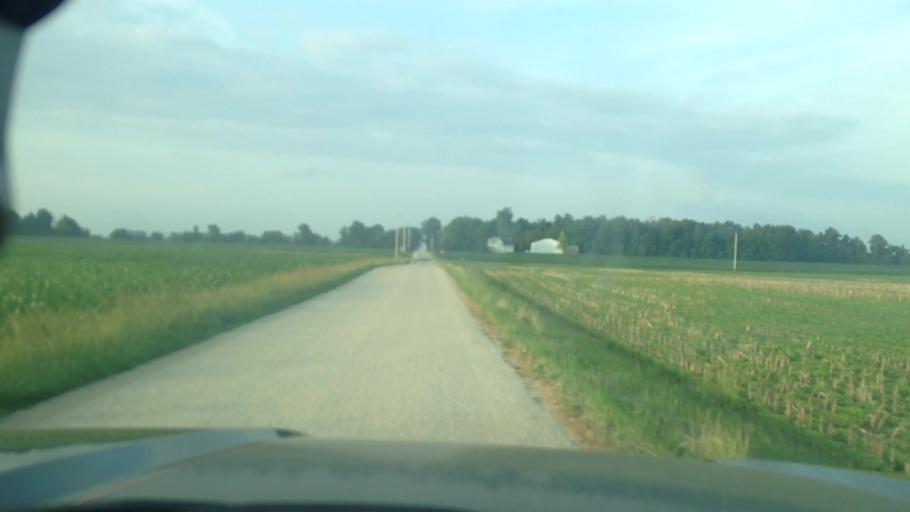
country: US
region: Indiana
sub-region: Randolph County
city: Union City
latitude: 40.2459
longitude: -84.8624
